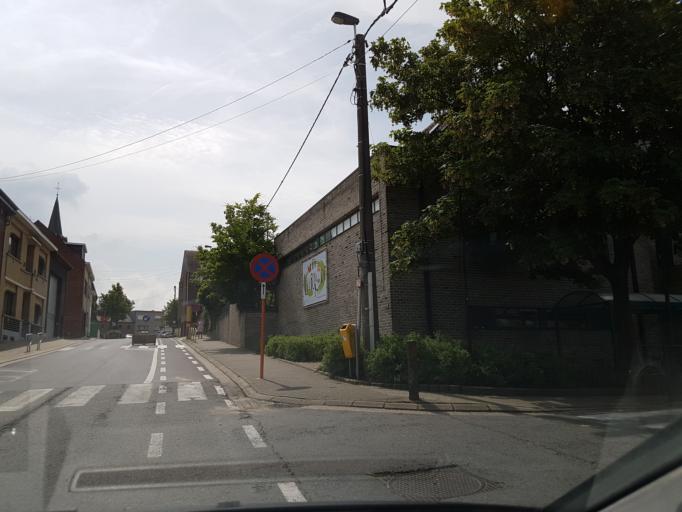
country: BE
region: Flanders
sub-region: Provincie Vlaams-Brabant
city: Asse
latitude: 50.9193
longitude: 4.1563
